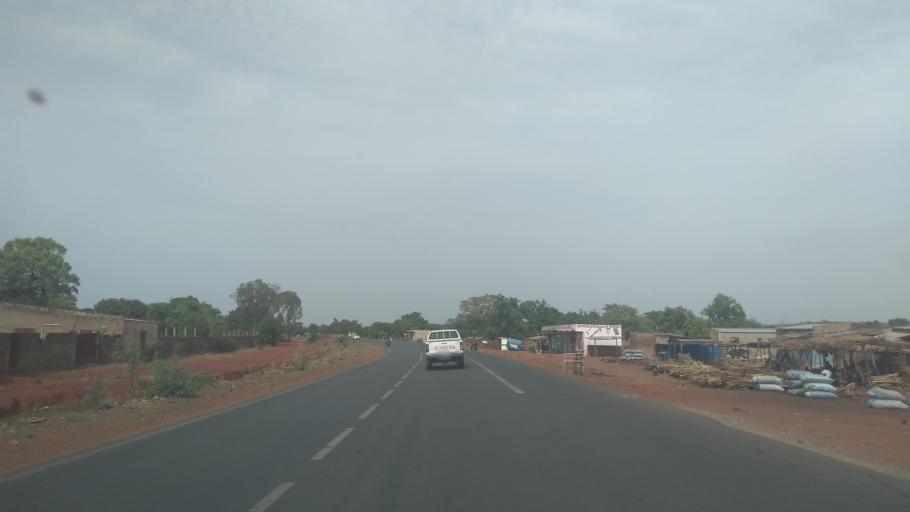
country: ML
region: Bamako
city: Bamako
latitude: 12.5796
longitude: -7.7809
